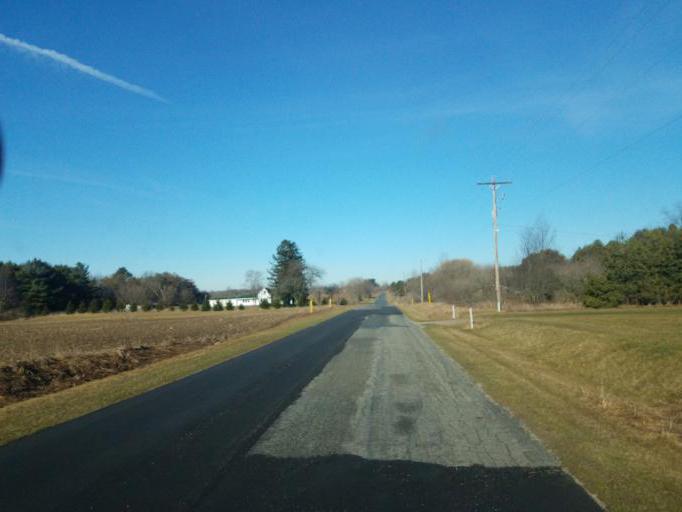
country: US
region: Michigan
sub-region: Montcalm County
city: Edmore
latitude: 43.4226
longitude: -85.0397
